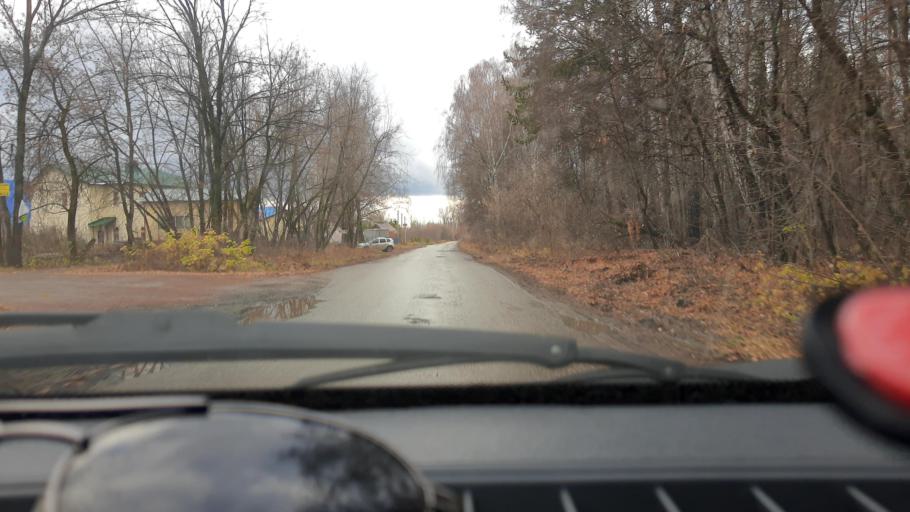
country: RU
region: Bashkortostan
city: Ufa
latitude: 54.7904
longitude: 56.1578
